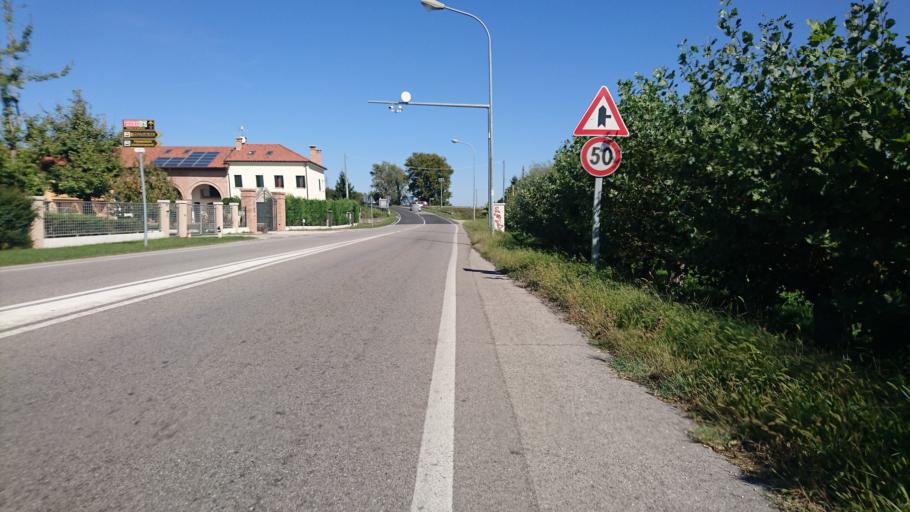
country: IT
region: Veneto
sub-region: Provincia di Venezia
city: Fosso
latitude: 45.3991
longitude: 12.0520
